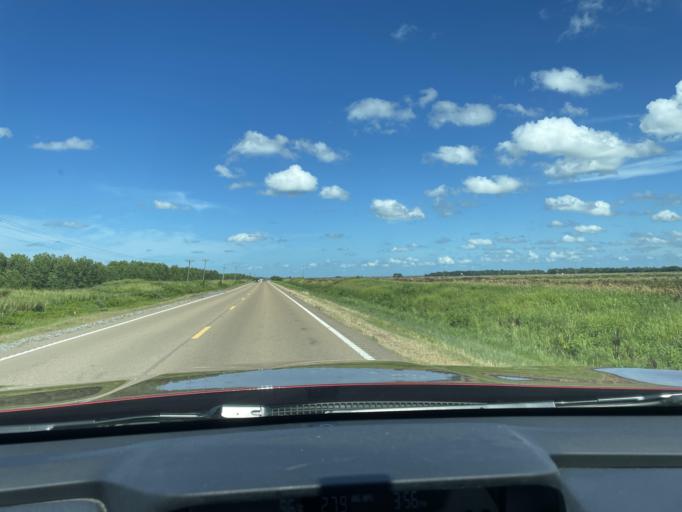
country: US
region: Mississippi
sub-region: Humphreys County
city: Belzoni
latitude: 33.1827
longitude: -90.6233
